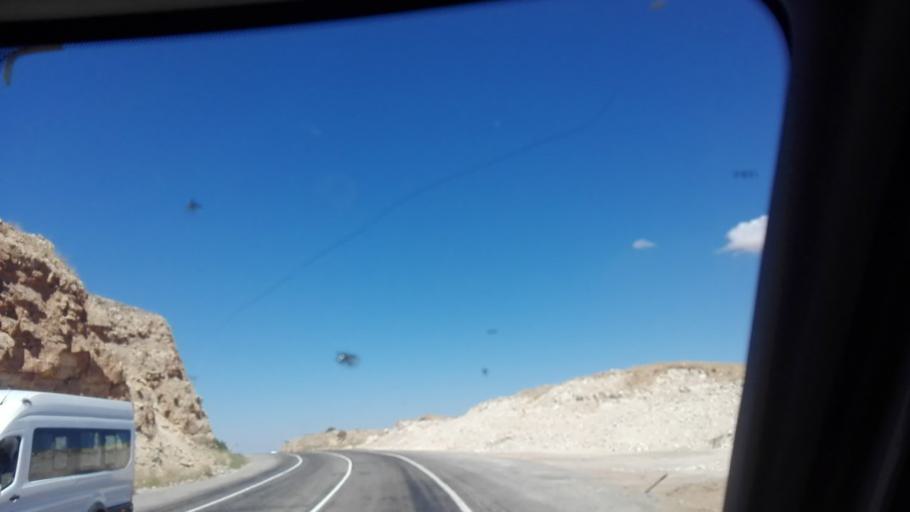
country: TR
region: Batman
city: Gerdzhyush
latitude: 37.5566
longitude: 41.3632
